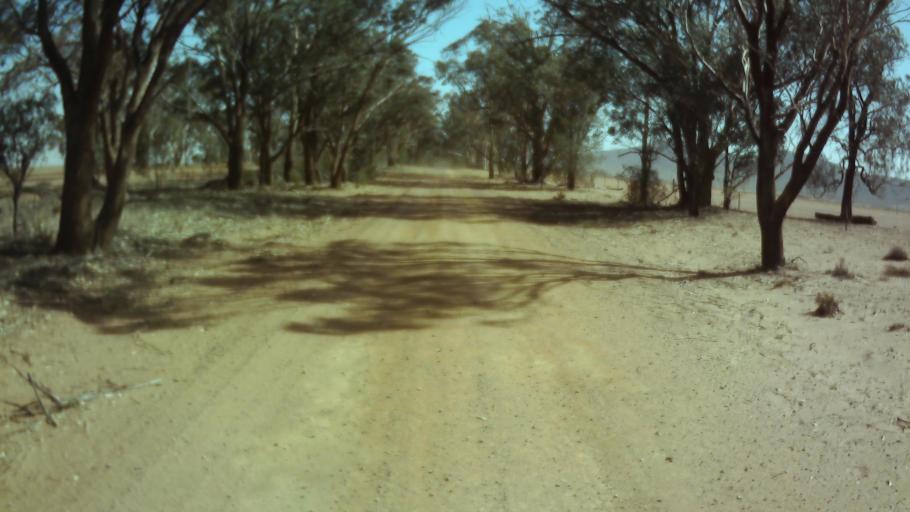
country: AU
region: New South Wales
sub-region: Weddin
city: Grenfell
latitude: -33.8466
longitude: 148.0171
